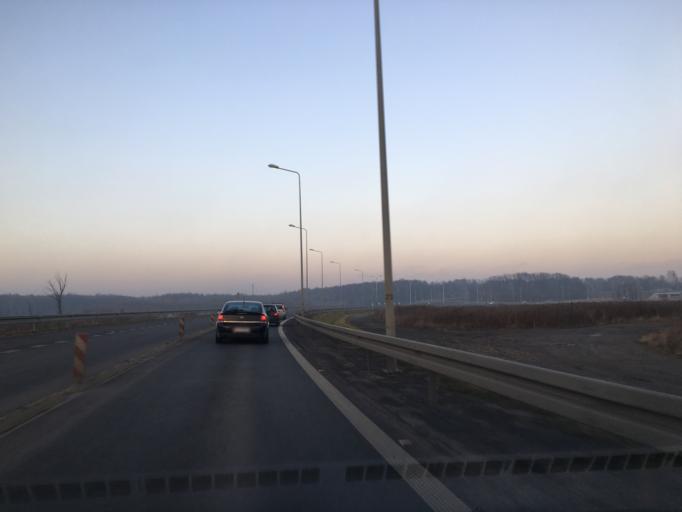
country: PL
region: Silesian Voivodeship
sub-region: Powiat tarnogorski
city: Radzionkow
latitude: 50.3643
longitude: 18.8702
